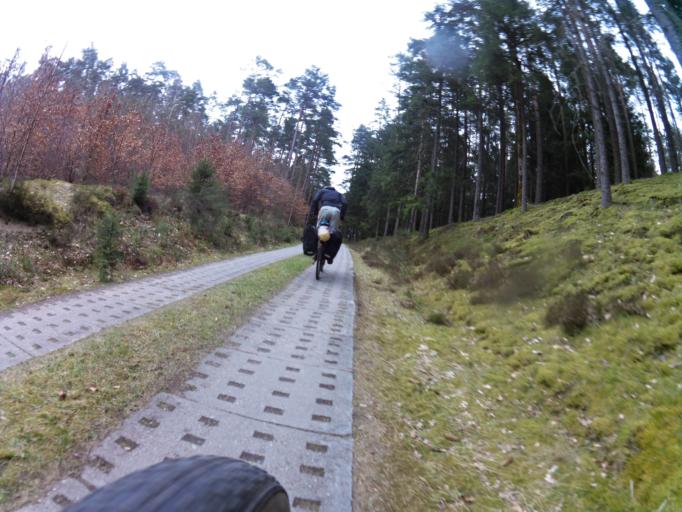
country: PL
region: West Pomeranian Voivodeship
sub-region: Powiat koszalinski
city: Polanow
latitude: 54.1798
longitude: 16.6662
